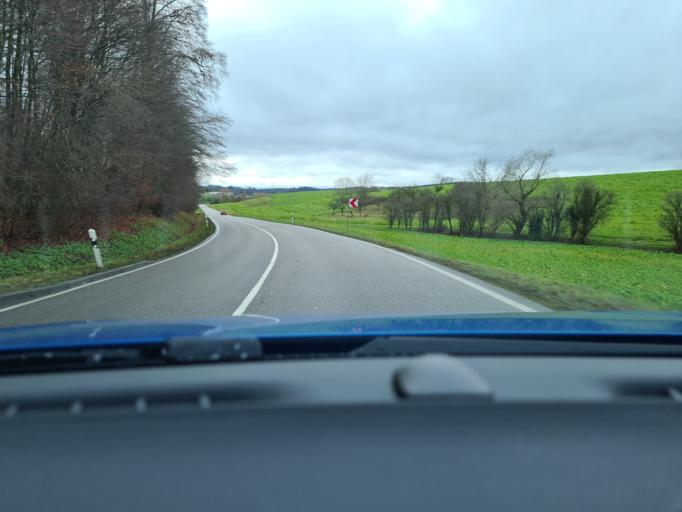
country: DE
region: Baden-Wuerttemberg
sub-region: Karlsruhe Region
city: Mauer
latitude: 49.3239
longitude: 8.7771
